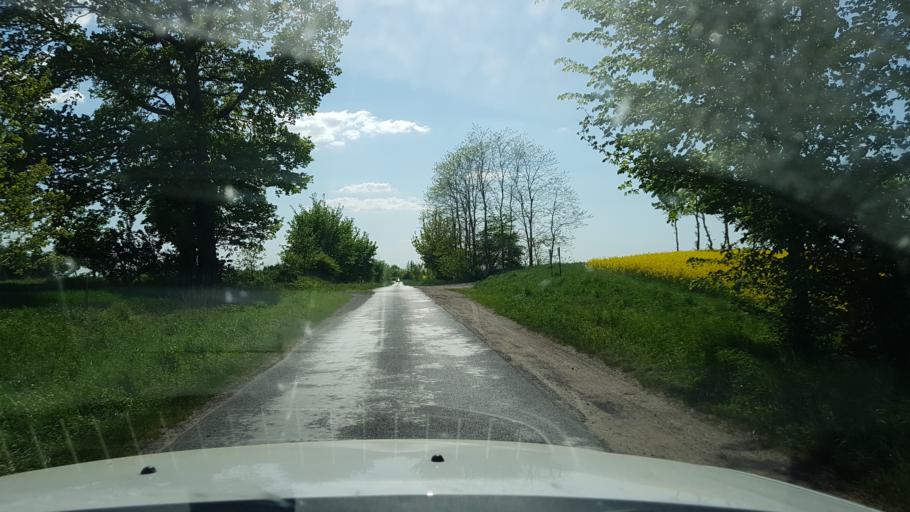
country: PL
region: West Pomeranian Voivodeship
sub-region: Powiat kolobrzeski
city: Goscino
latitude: 54.0203
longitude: 15.6305
